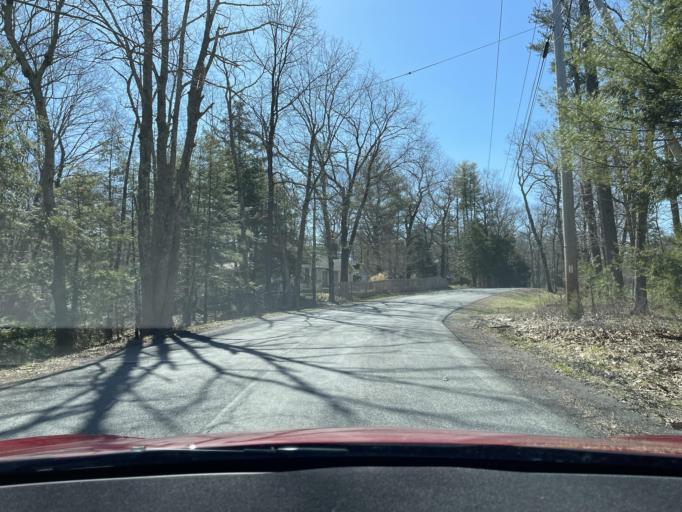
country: US
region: New York
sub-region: Ulster County
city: Manorville
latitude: 42.0729
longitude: -74.0241
